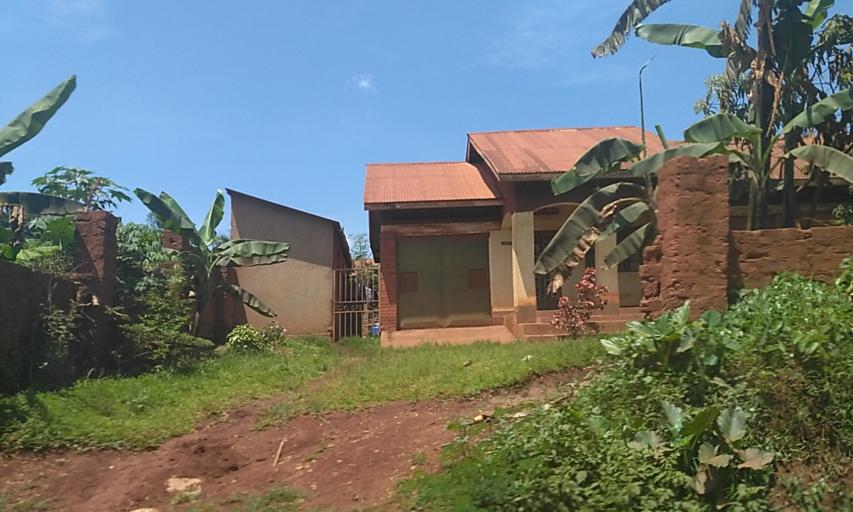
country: UG
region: Central Region
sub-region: Wakiso District
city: Wakiso
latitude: 0.4017
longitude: 32.4863
